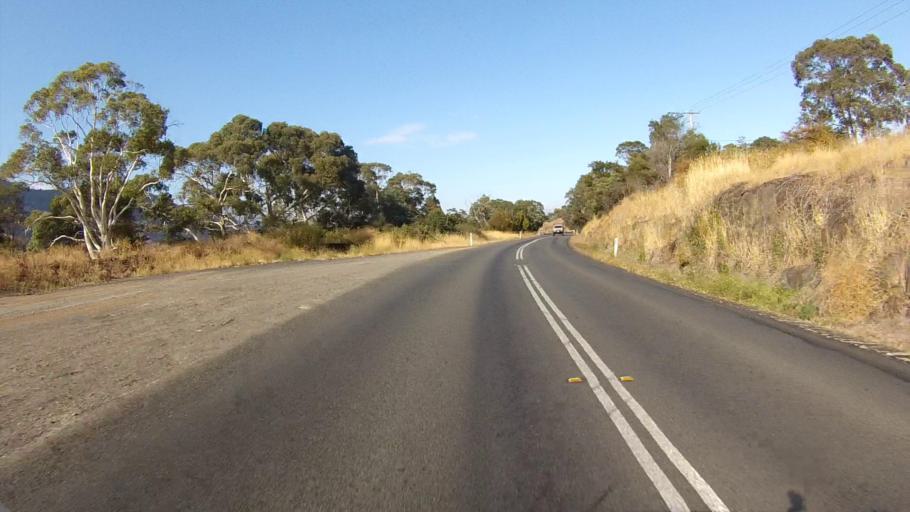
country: AU
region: Tasmania
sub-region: Glenorchy
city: Granton
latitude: -42.7566
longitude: 147.1422
